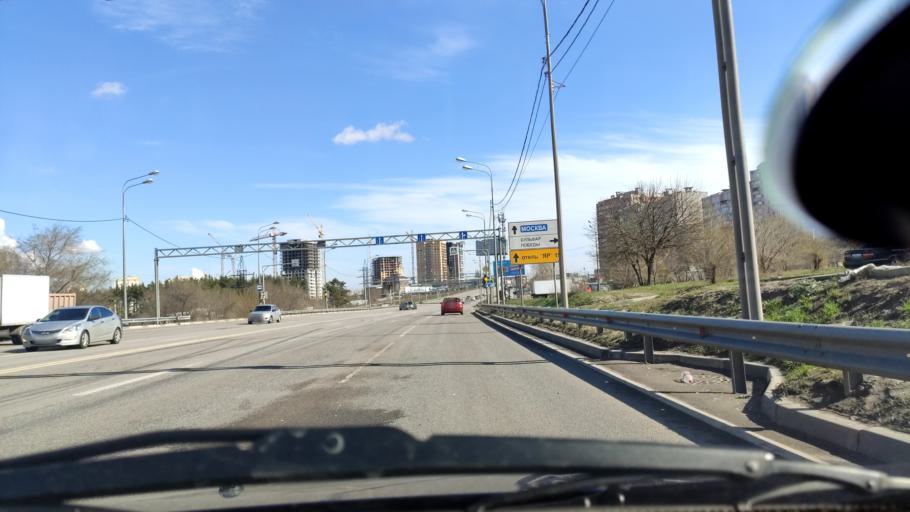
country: RU
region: Voronezj
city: Podgornoye
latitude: 51.7138
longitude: 39.1385
